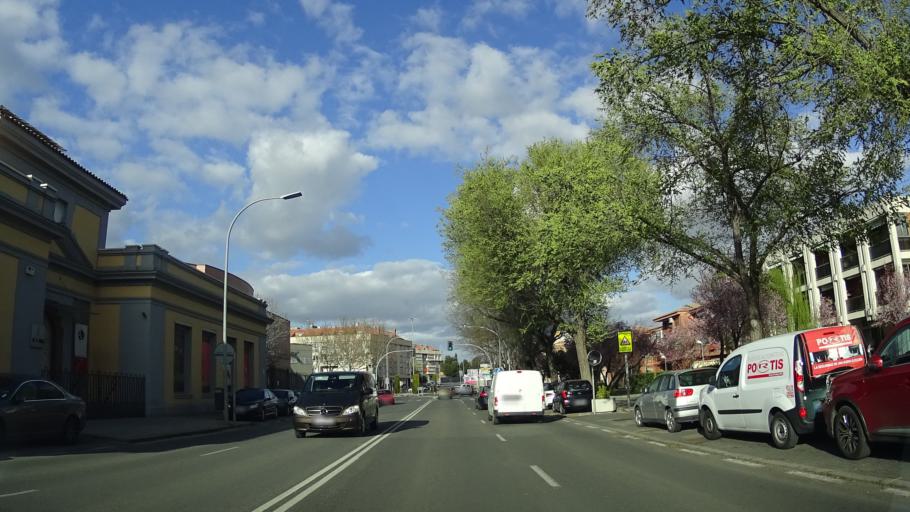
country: ES
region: Castille-La Mancha
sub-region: Provincia de Ciudad Real
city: Ciudad Real
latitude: 38.9810
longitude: -3.9260
